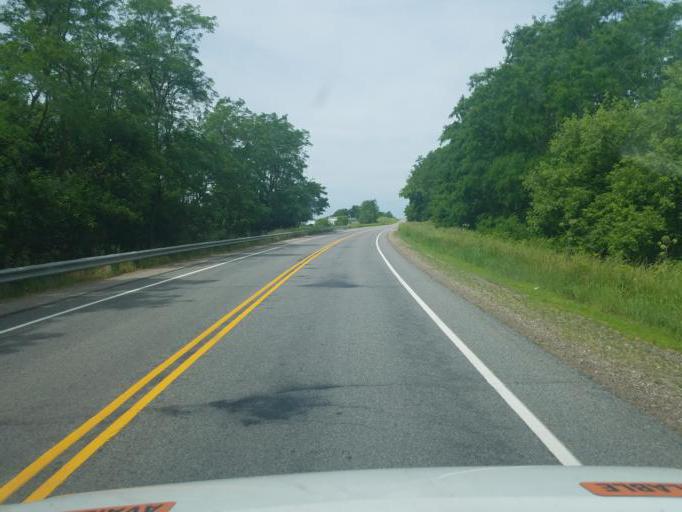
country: US
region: Wisconsin
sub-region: Juneau County
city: Elroy
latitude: 43.7748
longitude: -90.2083
